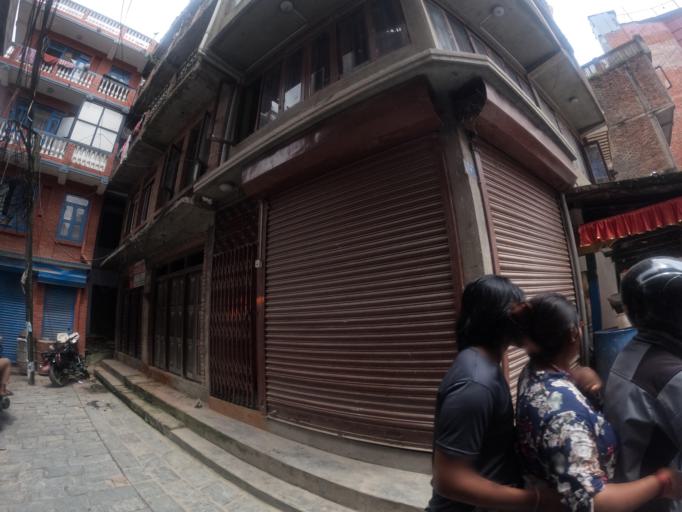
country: NP
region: Central Region
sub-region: Bagmati Zone
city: Bhaktapur
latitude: 27.6847
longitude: 85.3848
